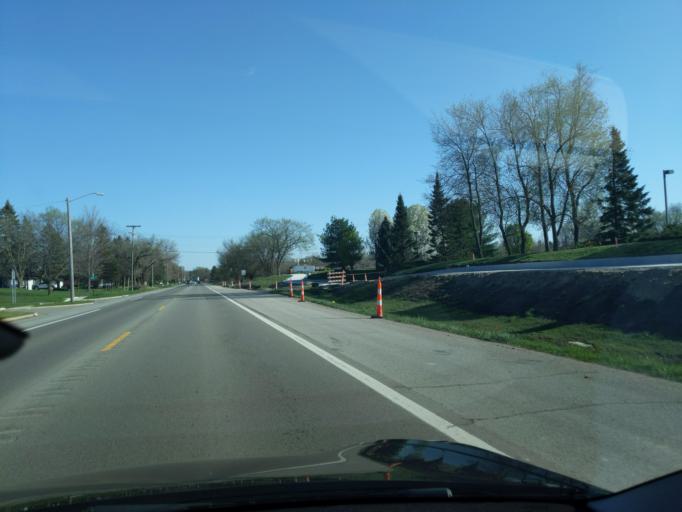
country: US
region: Michigan
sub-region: Washtenaw County
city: Chelsea
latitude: 42.3300
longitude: -84.0237
